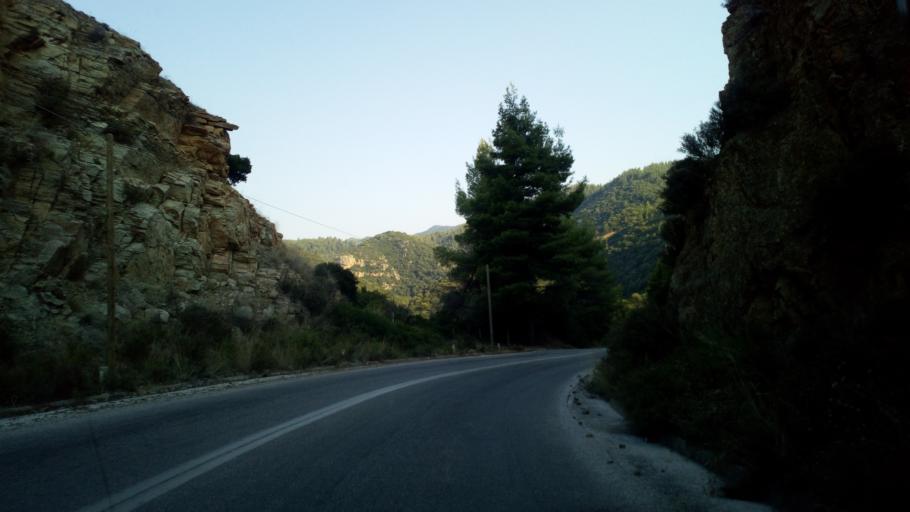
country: GR
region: Central Macedonia
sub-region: Nomos Chalkidikis
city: Neos Marmaras
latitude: 40.1742
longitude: 23.8499
